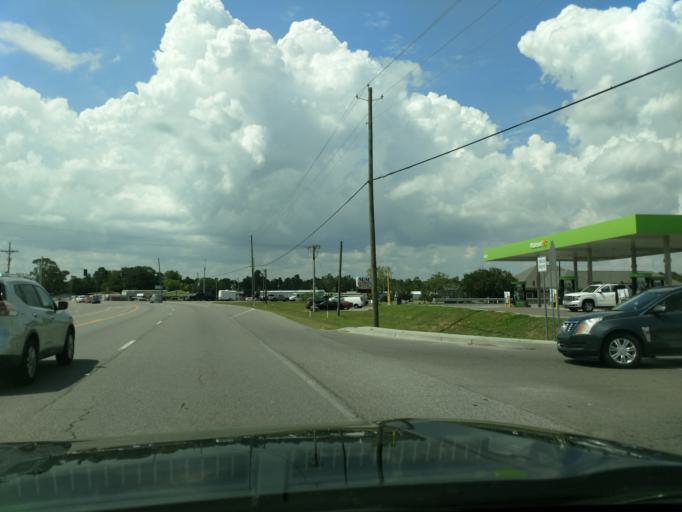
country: US
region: Mississippi
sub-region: Jackson County
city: Gulf Hills
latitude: 30.4343
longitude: -88.8301
